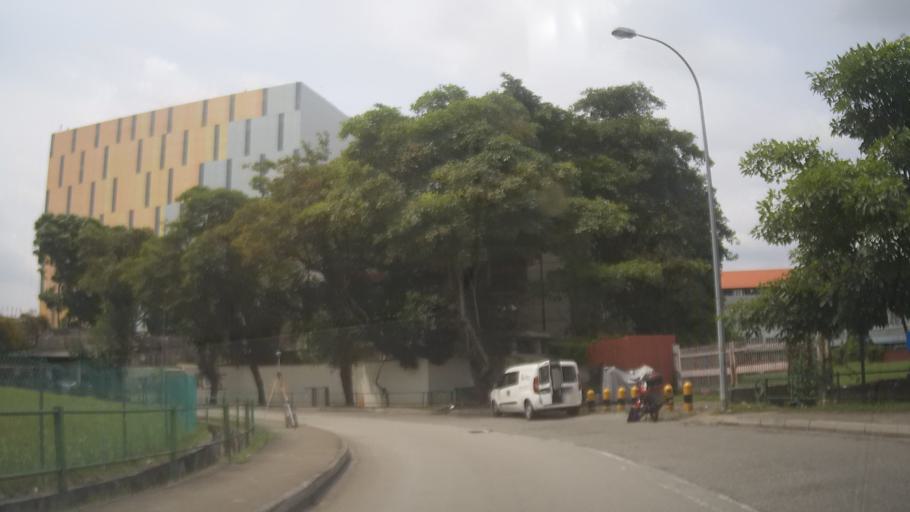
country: MY
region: Johor
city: Johor Bahru
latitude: 1.4140
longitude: 103.7474
